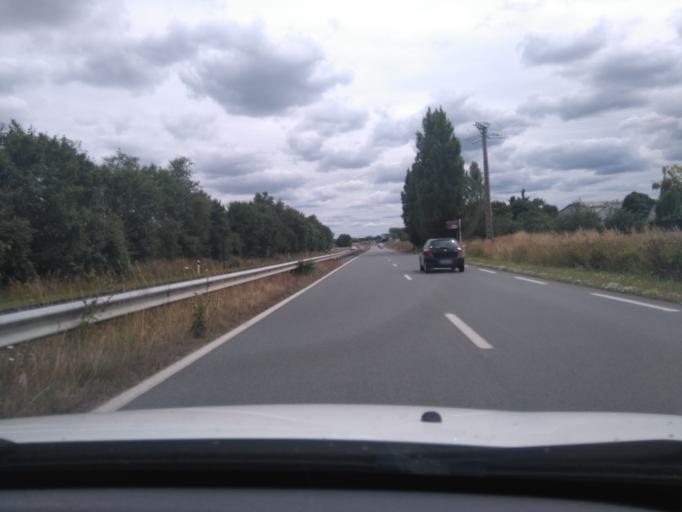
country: FR
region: Brittany
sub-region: Departement des Cotes-d'Armor
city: Cavan
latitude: 48.6509
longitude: -3.3303
